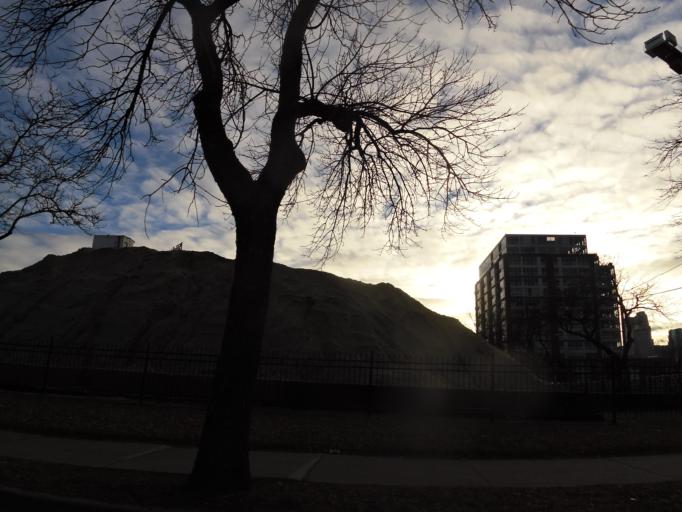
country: US
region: Minnesota
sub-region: Hennepin County
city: Minneapolis
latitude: 44.9856
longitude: -93.2519
